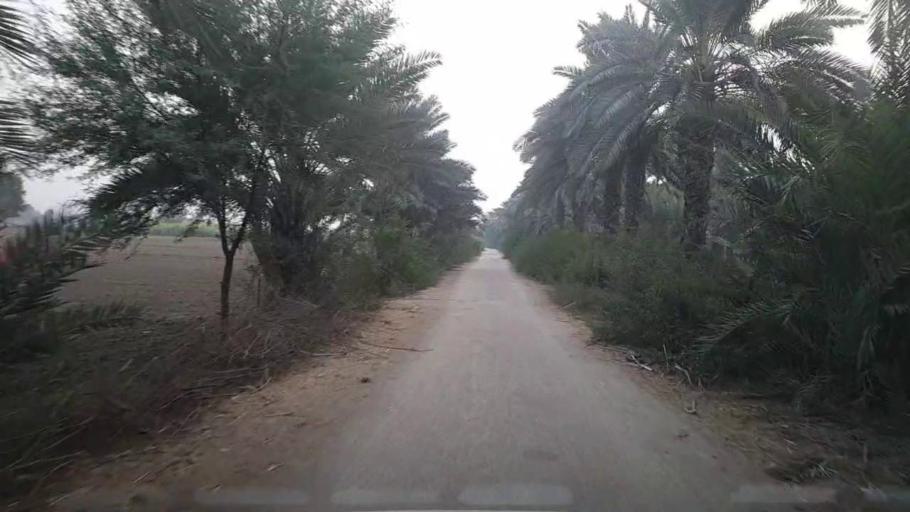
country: PK
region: Sindh
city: Kot Diji
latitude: 27.3315
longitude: 68.6404
